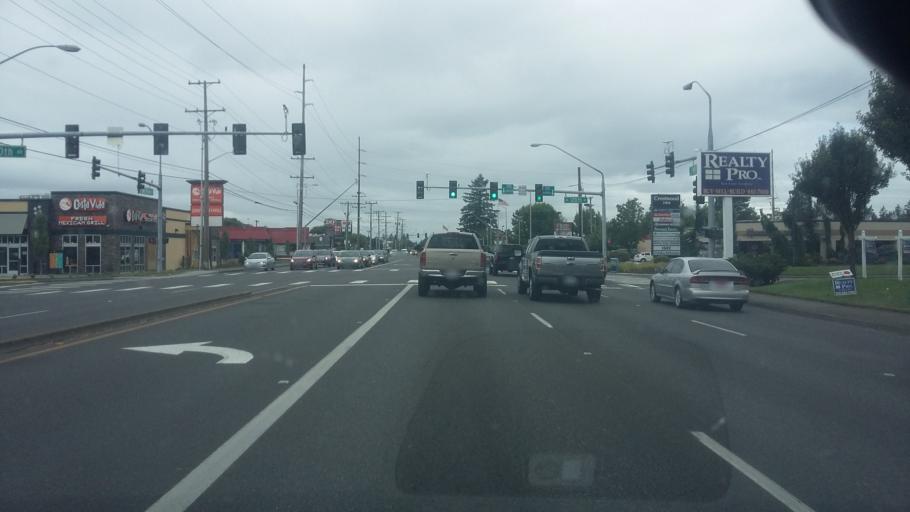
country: US
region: Washington
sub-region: Clark County
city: Orchards
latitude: 45.6204
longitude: -122.5488
